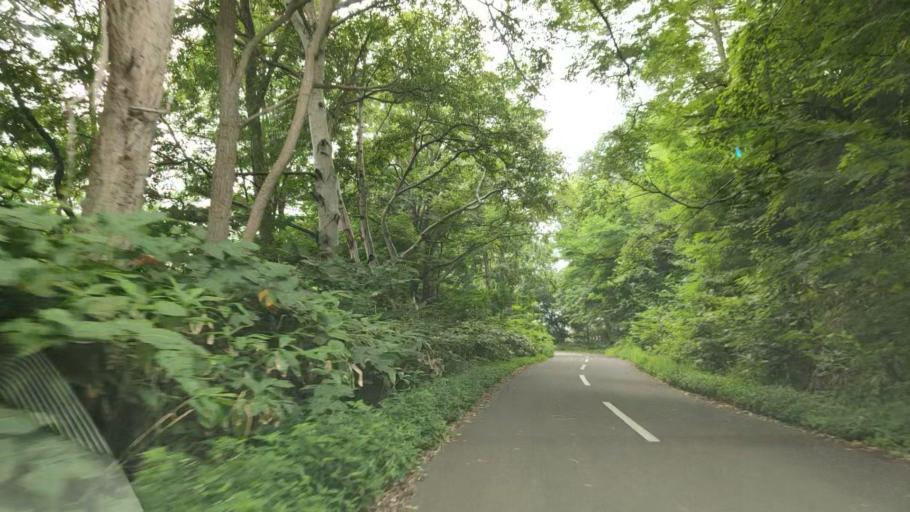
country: JP
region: Hokkaido
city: Otaru
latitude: 43.1928
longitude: 140.9849
